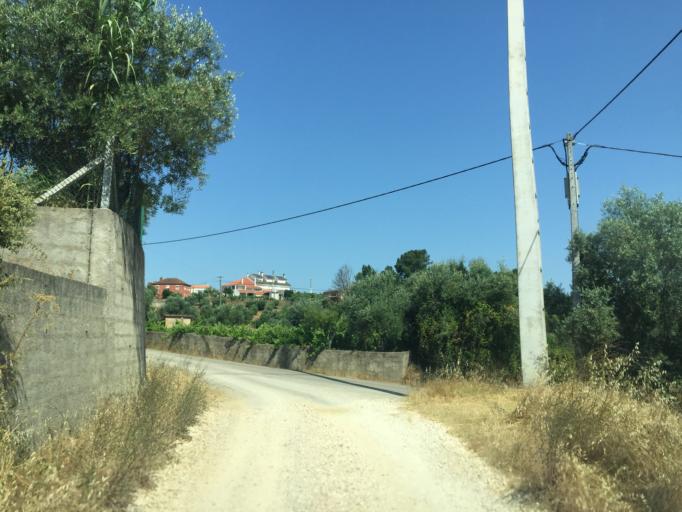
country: PT
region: Santarem
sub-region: Ferreira do Zezere
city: Ferreira do Zezere
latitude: 39.6065
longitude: -8.2836
